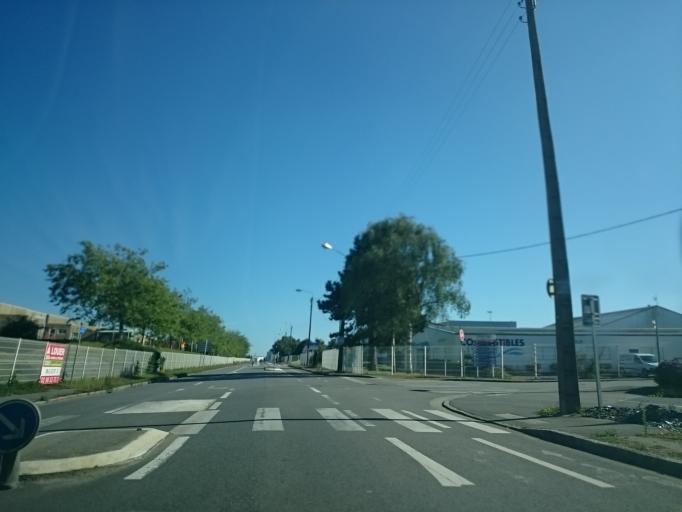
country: FR
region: Brittany
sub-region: Departement du Finistere
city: Brest
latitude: 48.4222
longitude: -4.4635
